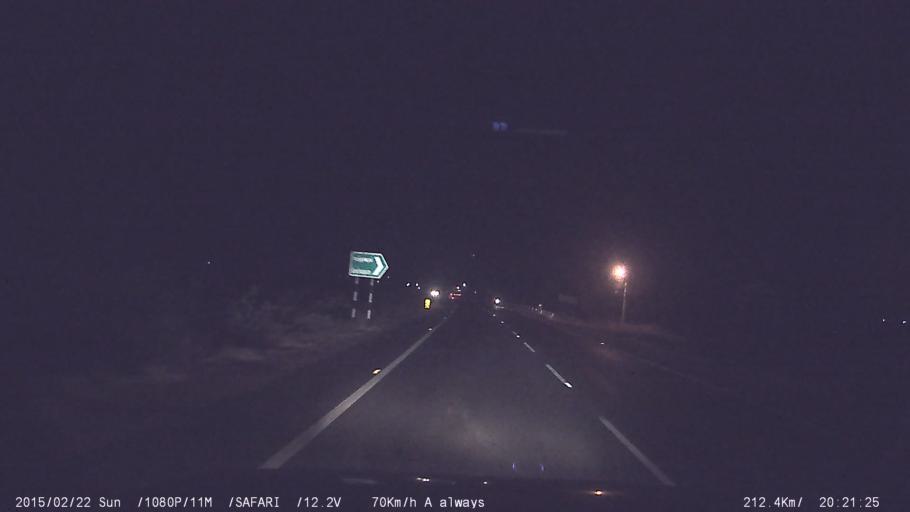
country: IN
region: Tamil Nadu
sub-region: Dindigul
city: Nilakottai
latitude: 10.2885
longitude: 77.8786
